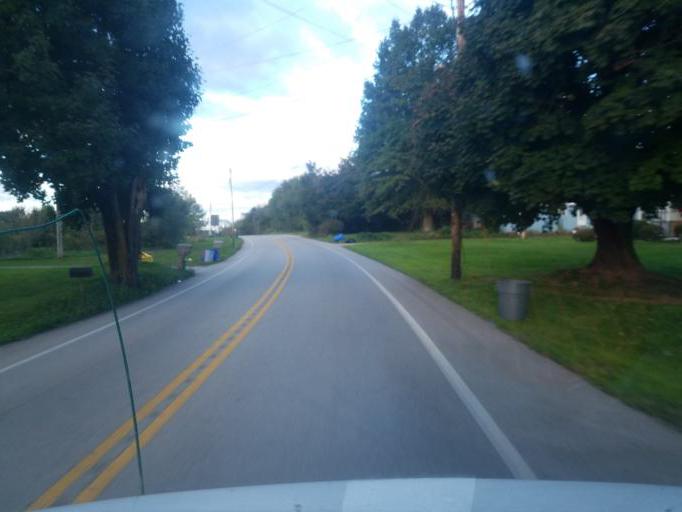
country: US
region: Pennsylvania
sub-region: York County
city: Spring Grove
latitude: 39.9397
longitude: -76.8946
